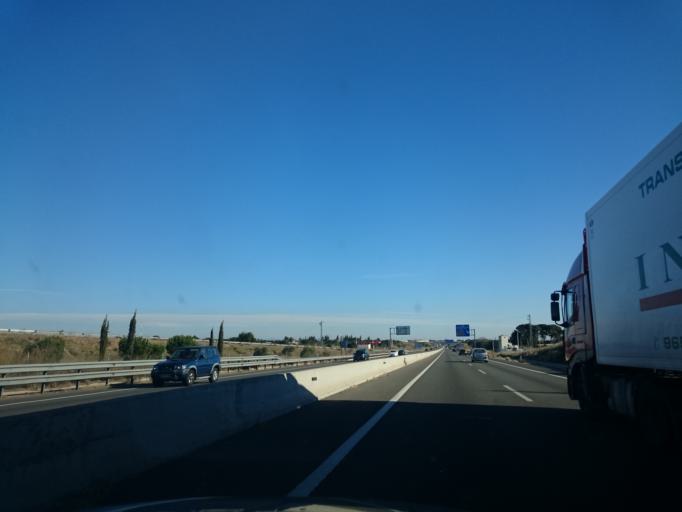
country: ES
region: Catalonia
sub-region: Provincia de Tarragona
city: Salou
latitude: 41.0956
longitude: 1.1092
